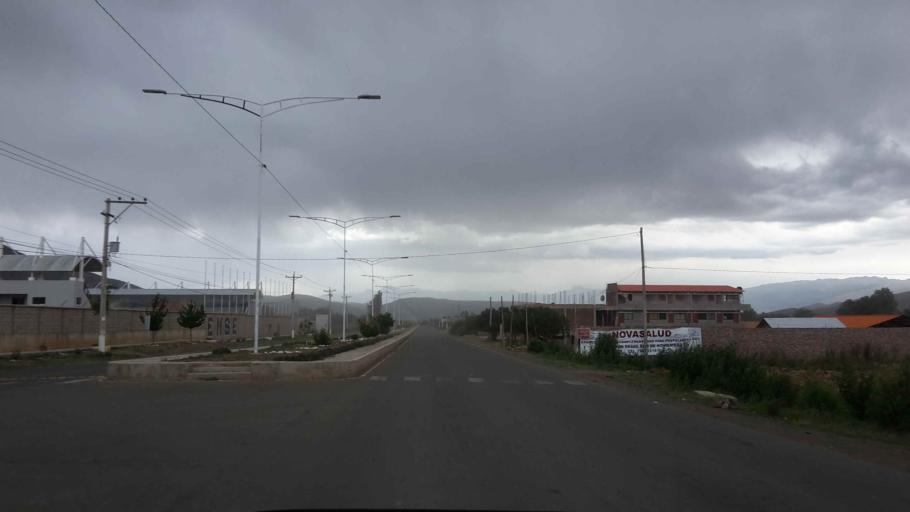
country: BO
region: Cochabamba
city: Tarata
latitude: -17.5987
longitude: -66.0374
